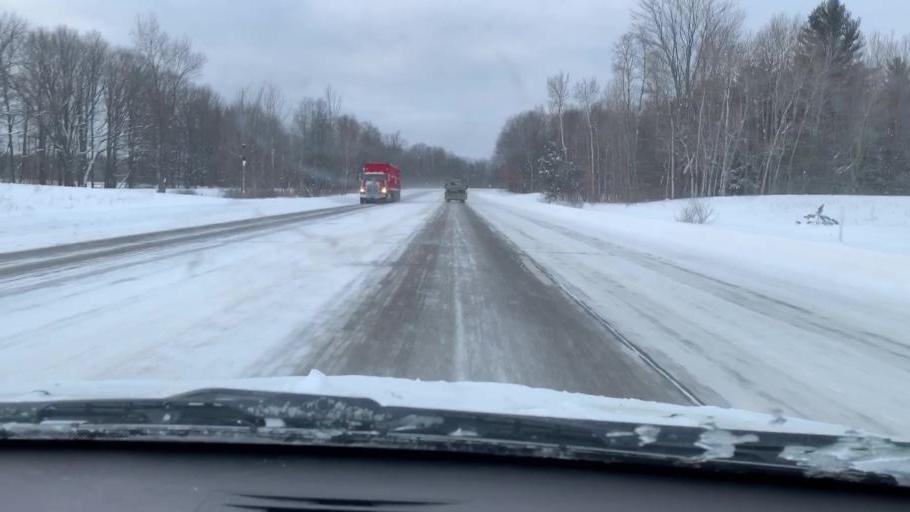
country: US
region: Michigan
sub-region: Kalkaska County
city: Kalkaska
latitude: 44.6177
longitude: -85.3027
